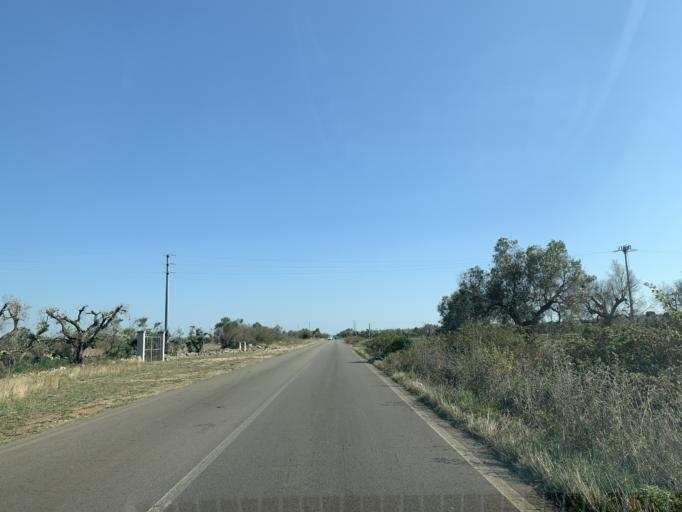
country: IT
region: Apulia
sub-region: Provincia di Lecce
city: Copertino
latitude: 40.2581
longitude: 18.0206
